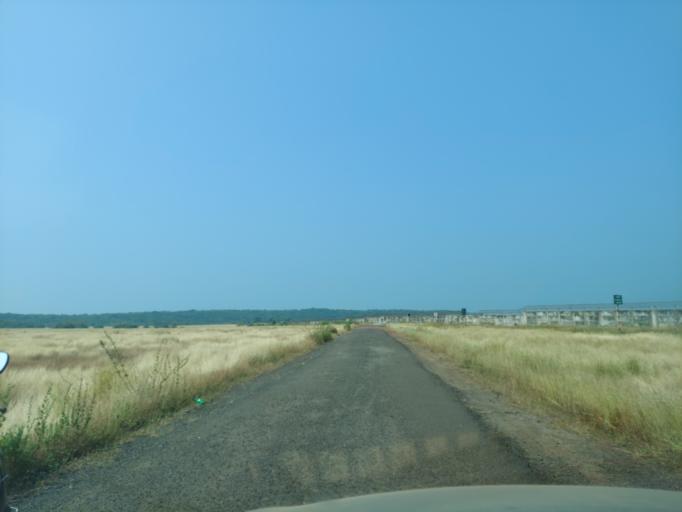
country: IN
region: Maharashtra
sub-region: Sindhudurg
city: Malvan
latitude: 15.9983
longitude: 73.5138
